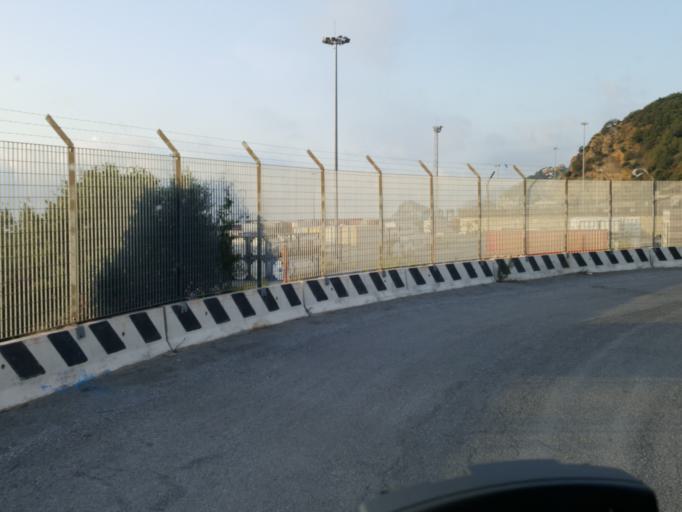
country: IT
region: Liguria
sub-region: Provincia di Savona
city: Bergeggi
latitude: 44.2575
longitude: 8.4531
